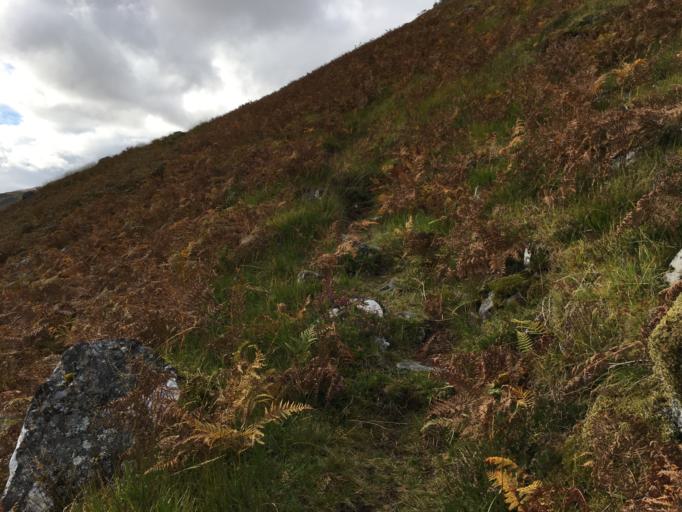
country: GB
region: Scotland
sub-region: Highland
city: Spean Bridge
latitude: 57.3315
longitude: -5.0480
